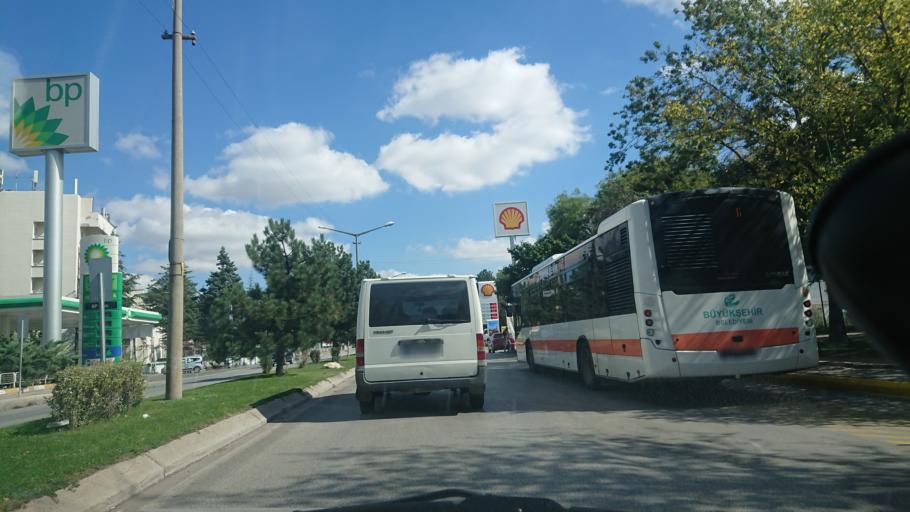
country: TR
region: Eskisehir
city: Eskisehir
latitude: 39.7639
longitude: 30.5566
